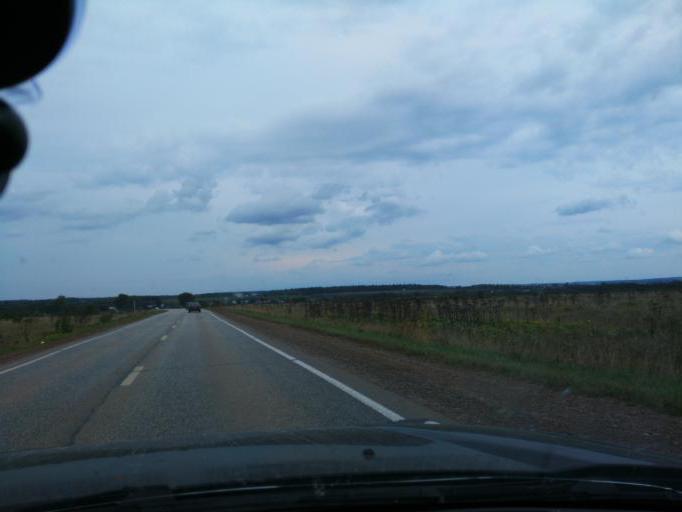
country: RU
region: Perm
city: Chernushka
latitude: 56.5083
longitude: 56.0012
